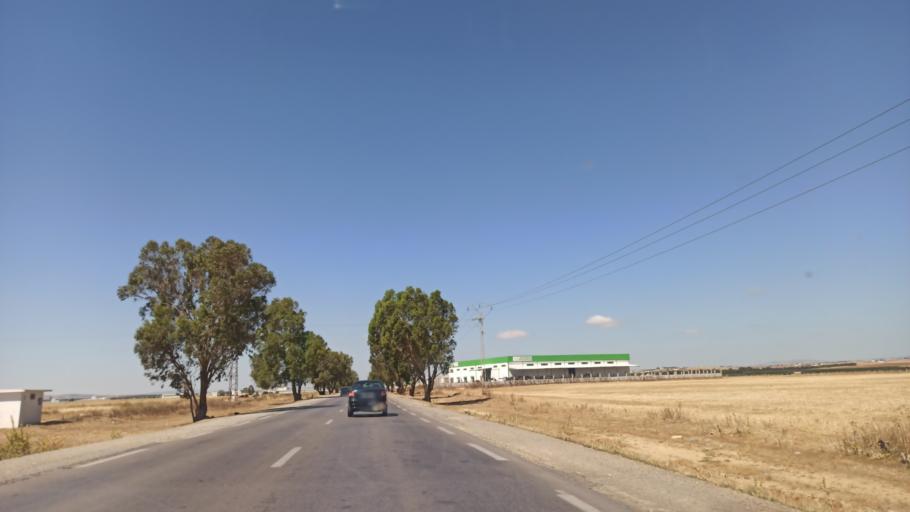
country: TN
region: Manouba
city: El Battan
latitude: 36.7405
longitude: 9.9541
